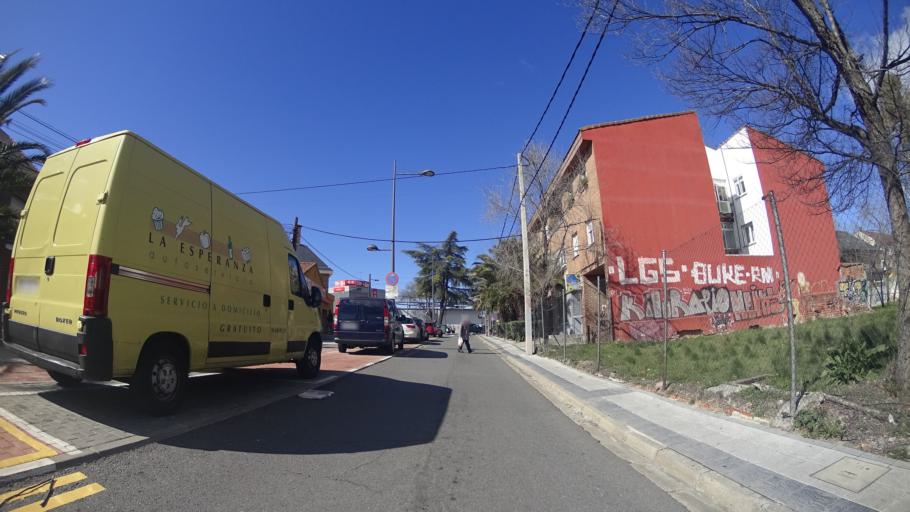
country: ES
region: Madrid
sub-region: Provincia de Madrid
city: Las Matas
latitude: 40.5526
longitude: -3.8956
